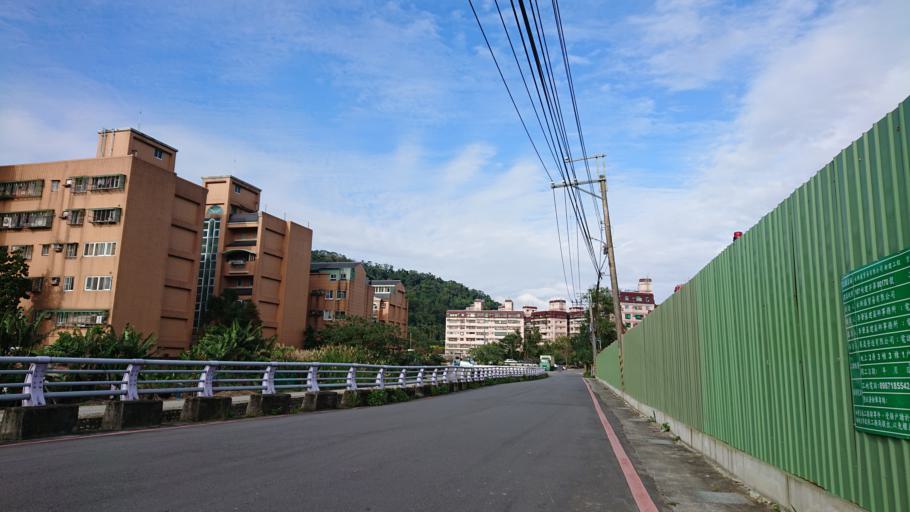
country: TW
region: Taiwan
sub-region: Taoyuan
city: Taoyuan
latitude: 24.9237
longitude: 121.3637
